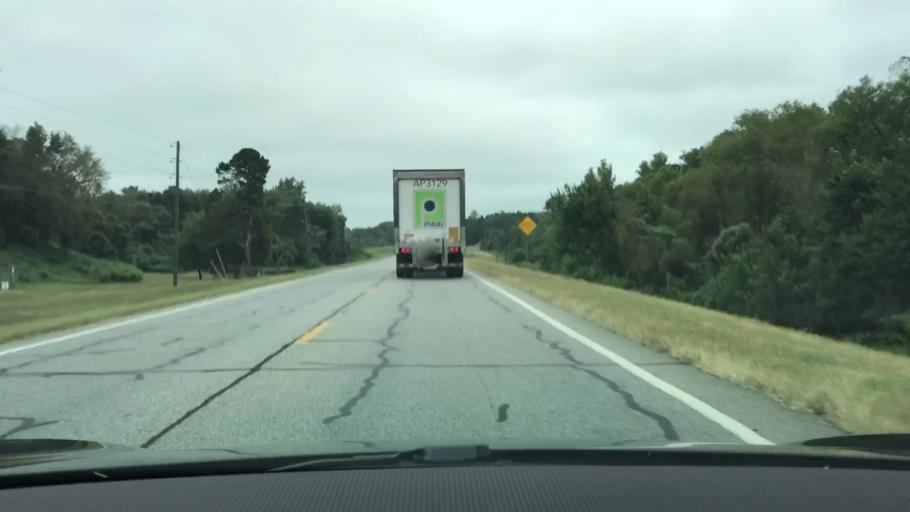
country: US
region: Georgia
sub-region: Oconee County
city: Watkinsville
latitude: 33.7326
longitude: -83.3030
